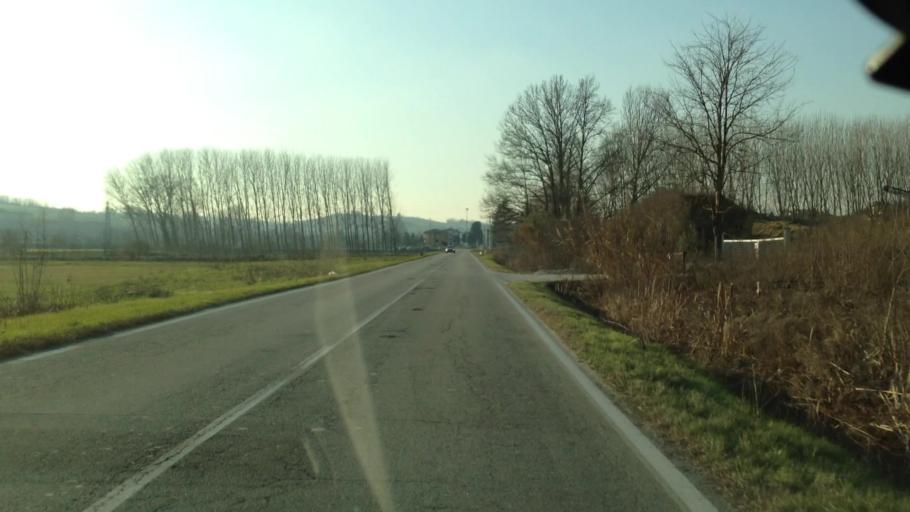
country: IT
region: Piedmont
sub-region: Provincia di Asti
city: Montaldo Scarampi
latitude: 44.8167
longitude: 8.2620
